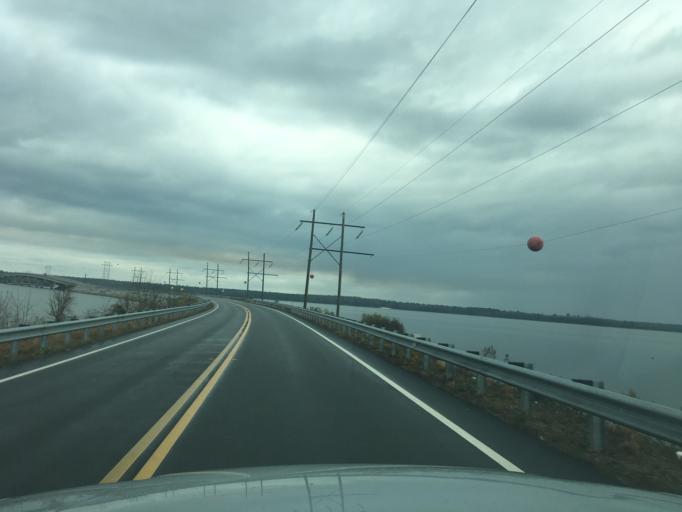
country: US
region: Georgia
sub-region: Columbia County
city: Appling
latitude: 33.6876
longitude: -82.3338
